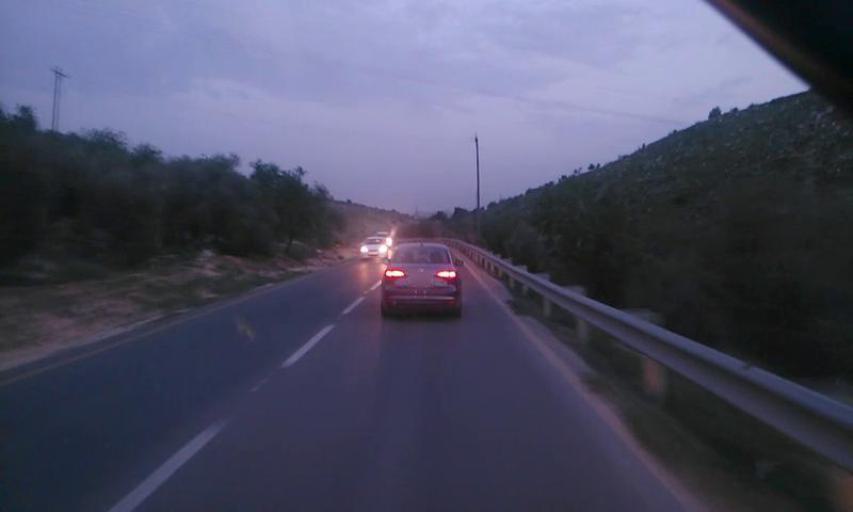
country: PS
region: West Bank
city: Ramin
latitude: 32.2811
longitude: 35.1442
